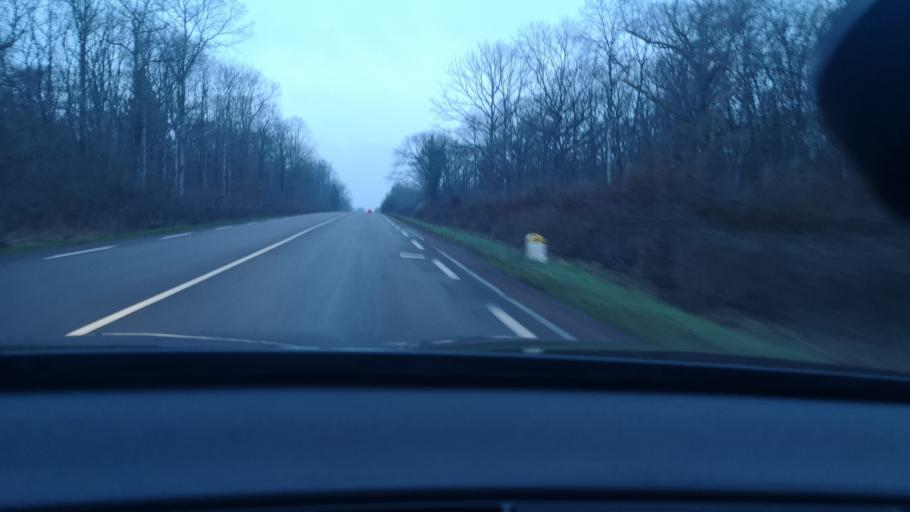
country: FR
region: Bourgogne
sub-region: Departement de Saone-et-Loire
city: Verdun-sur-le-Doubs
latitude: 47.0052
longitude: 5.0302
